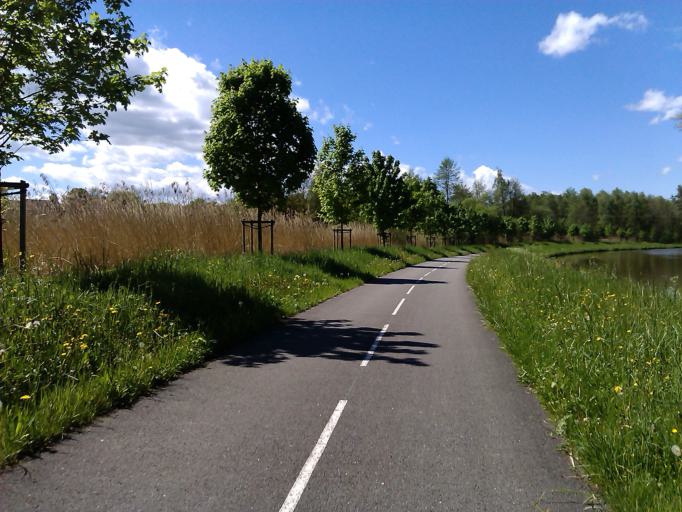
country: FR
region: Franche-Comte
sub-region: Territoire de Belfort
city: Montreux-Chateau
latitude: 47.5972
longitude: 6.9949
